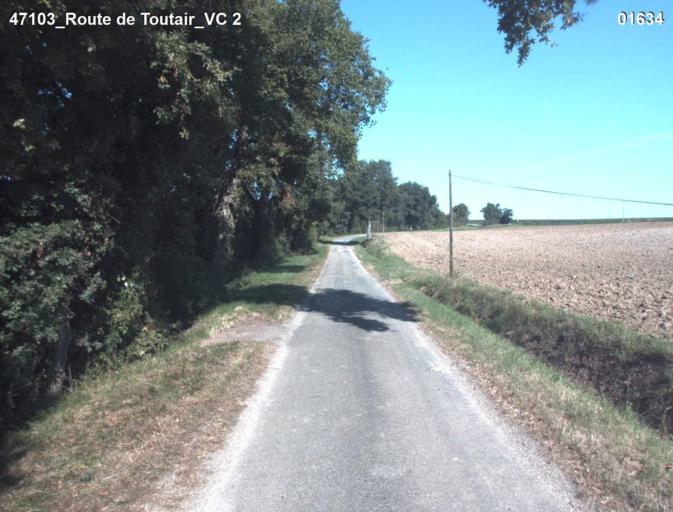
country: FR
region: Aquitaine
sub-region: Departement du Lot-et-Garonne
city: Nerac
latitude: 44.0739
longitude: 0.3311
